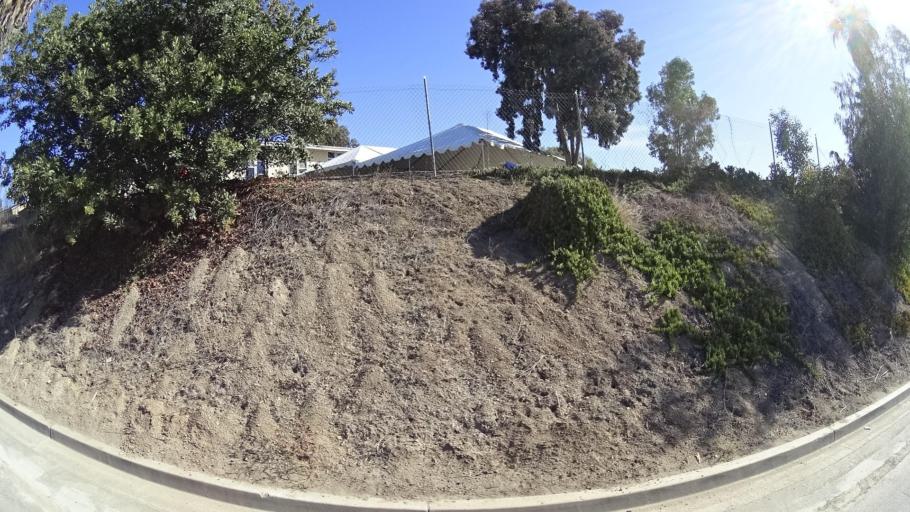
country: US
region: California
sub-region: San Diego County
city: La Presa
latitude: 32.7160
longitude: -117.0194
